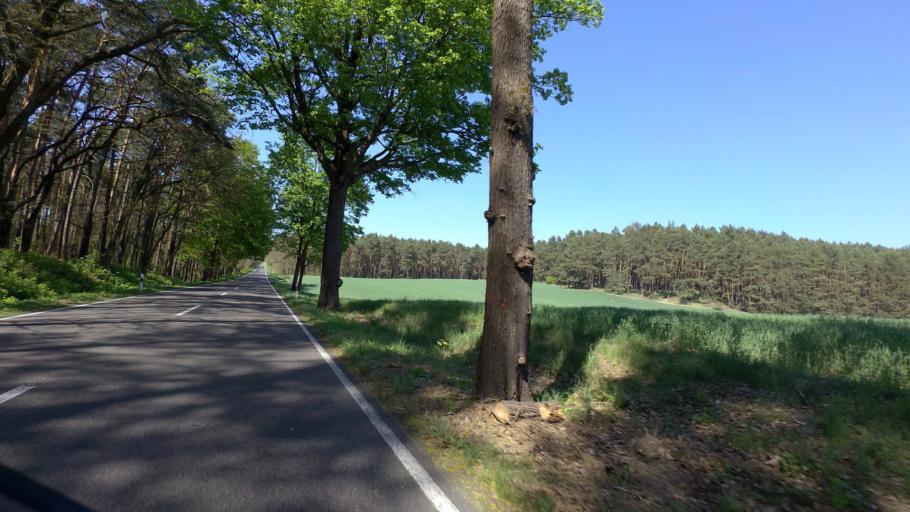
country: DE
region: Brandenburg
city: Lieberose
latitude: 52.0287
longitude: 14.3022
